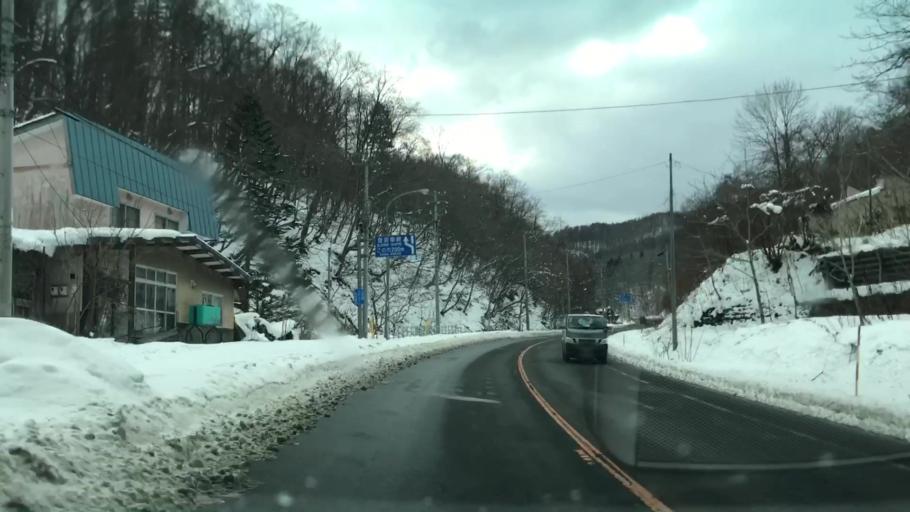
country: JP
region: Hokkaido
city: Yoichi
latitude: 43.2316
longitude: 140.7359
